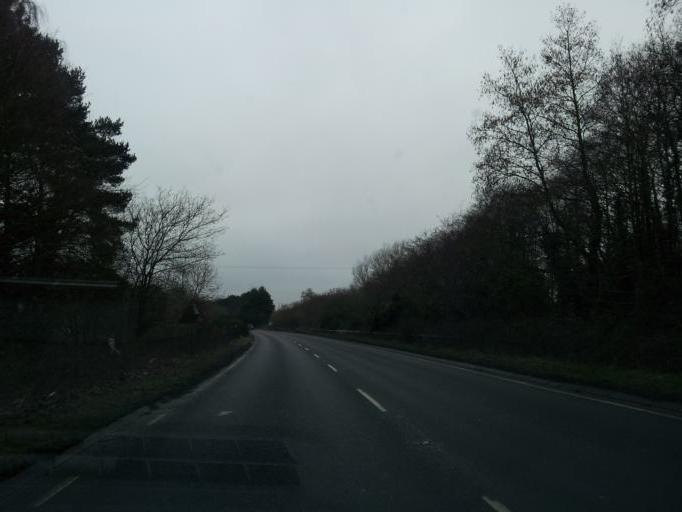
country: GB
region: England
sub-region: Suffolk
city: Ipswich
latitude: 52.0079
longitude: 1.1123
